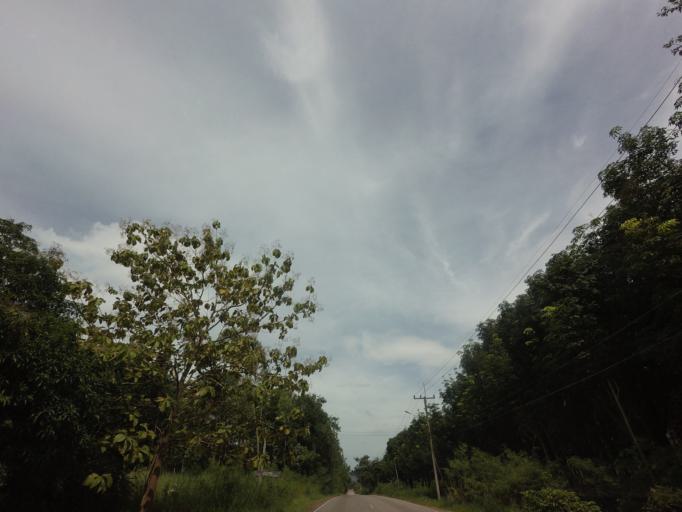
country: TH
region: Rayong
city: Klaeng
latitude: 12.6669
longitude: 101.5566
